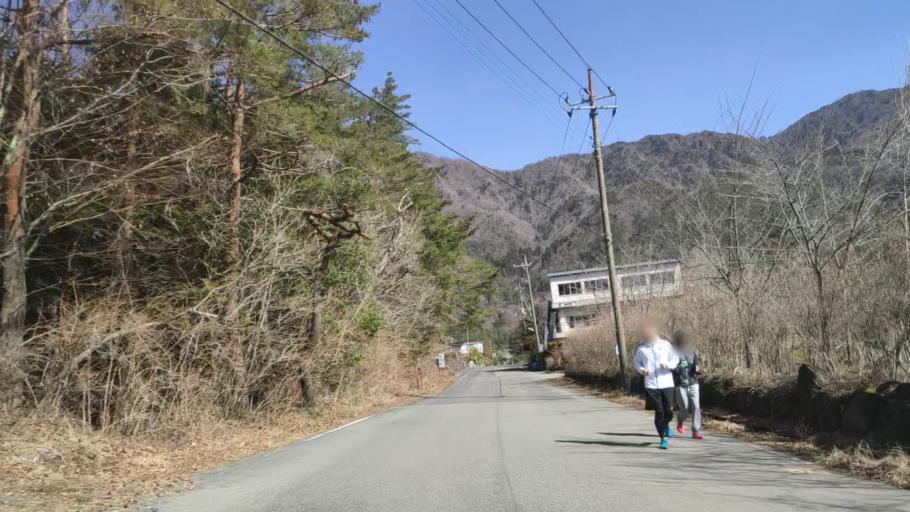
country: JP
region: Yamanashi
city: Fujikawaguchiko
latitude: 35.4993
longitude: 138.6623
